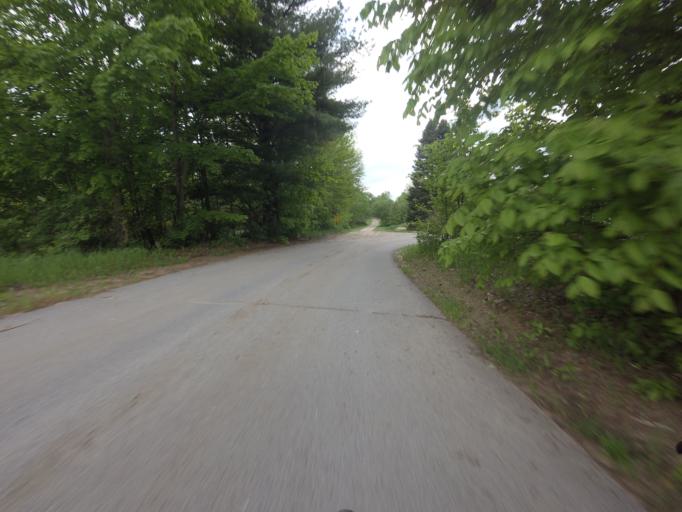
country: US
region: New York
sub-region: St. Lawrence County
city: Gouverneur
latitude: 44.1535
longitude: -75.3257
